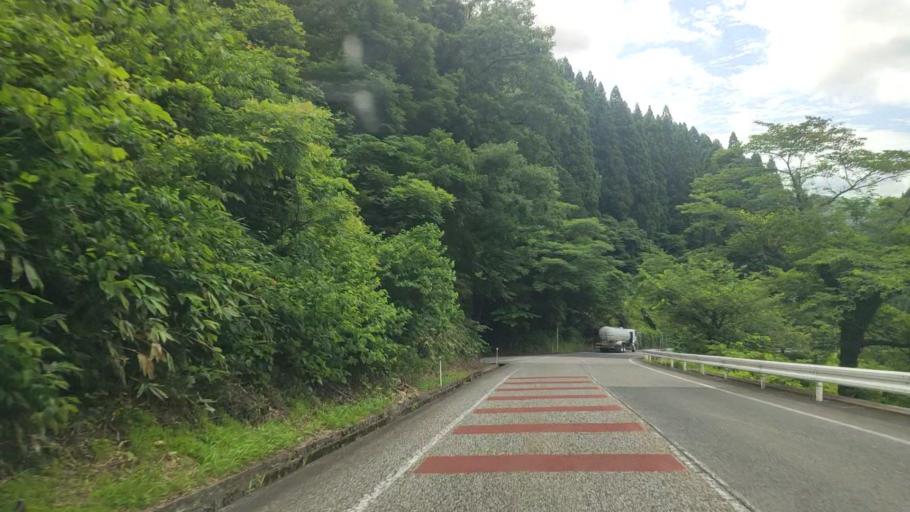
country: JP
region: Tottori
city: Yonago
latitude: 35.2545
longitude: 133.4380
